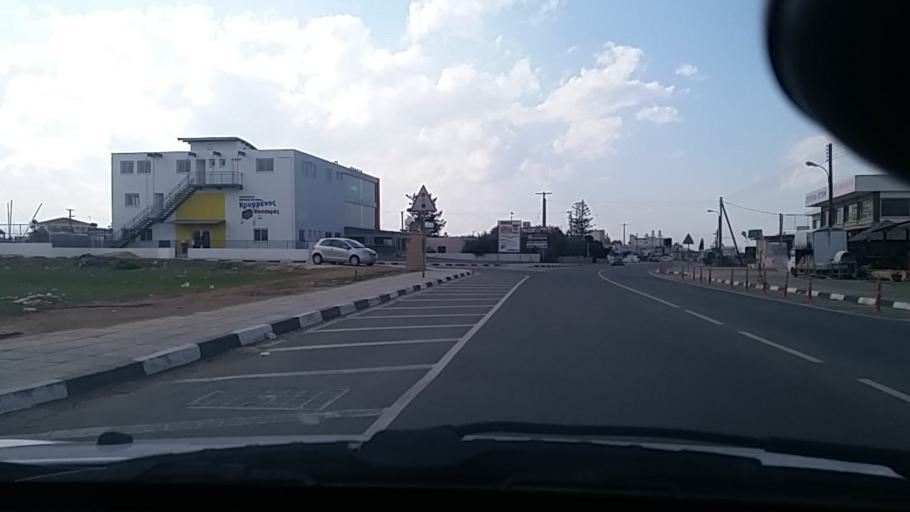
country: CY
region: Lefkosia
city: Kokkinotrimithia
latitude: 35.1484
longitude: 33.2082
